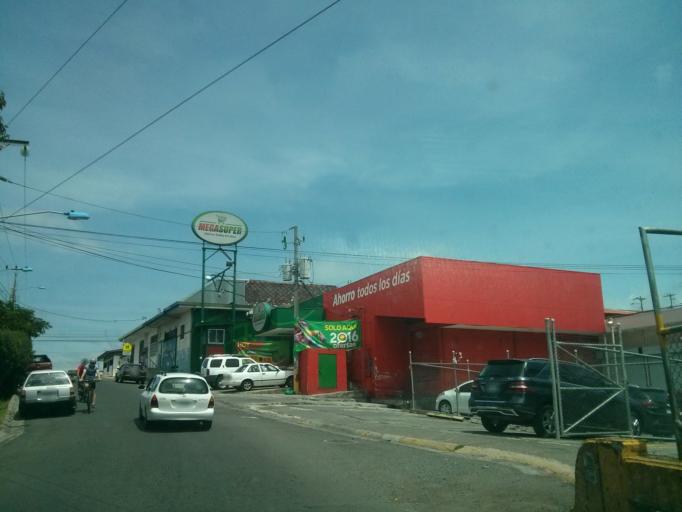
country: CR
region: Heredia
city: Angeles
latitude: 10.0179
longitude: -84.0540
